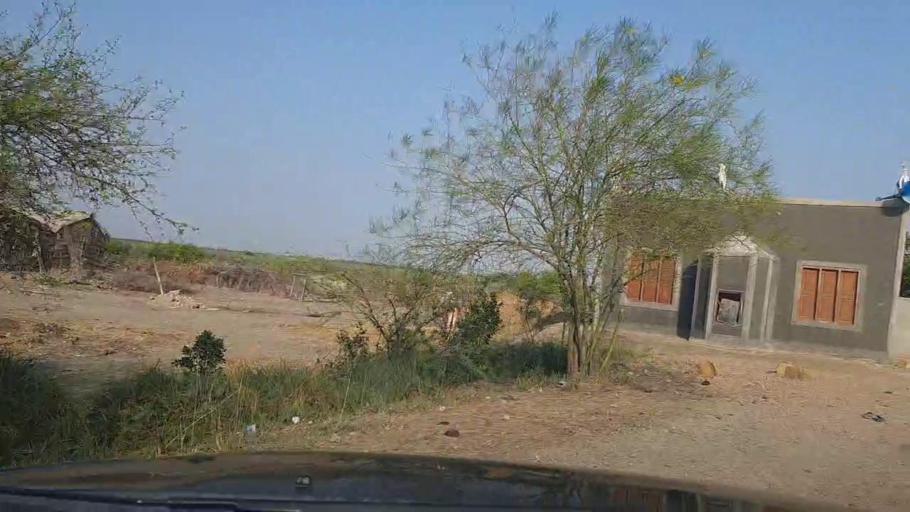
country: PK
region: Sindh
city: Mirpur Sakro
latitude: 24.6431
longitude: 67.7489
